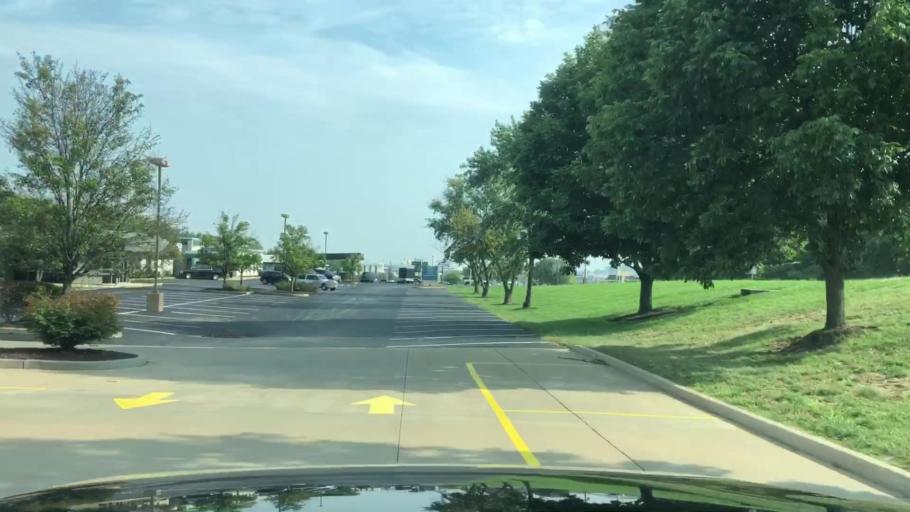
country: US
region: Missouri
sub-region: Saint Louis County
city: Woodson Terrace
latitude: 38.7279
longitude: -90.3583
